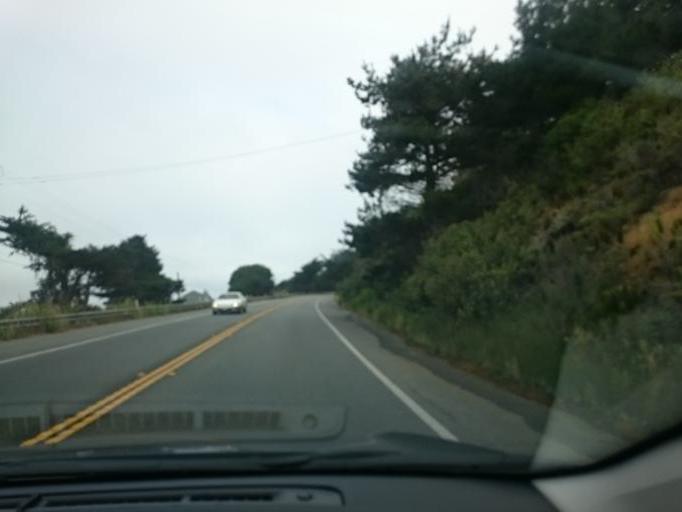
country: US
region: California
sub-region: San Mateo County
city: Moss Beach
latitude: 37.5301
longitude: -122.5159
